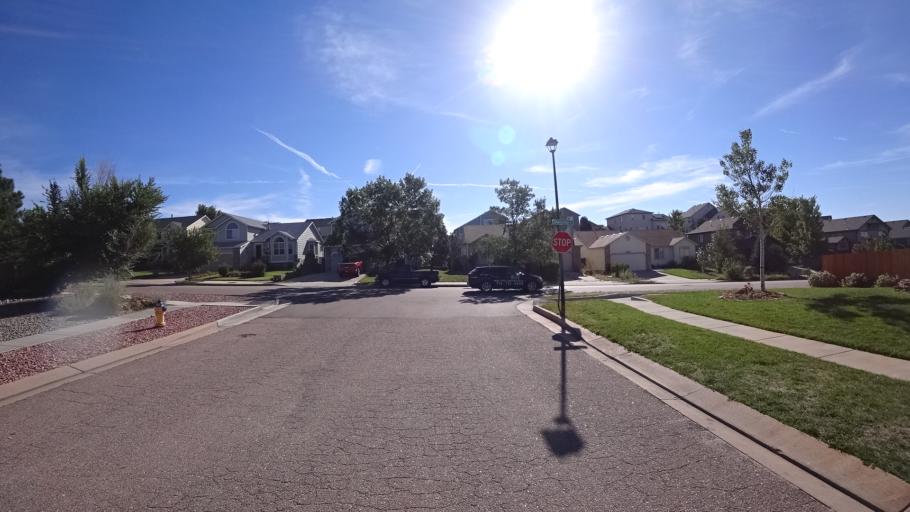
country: US
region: Colorado
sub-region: El Paso County
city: Black Forest
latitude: 38.9443
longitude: -104.7389
